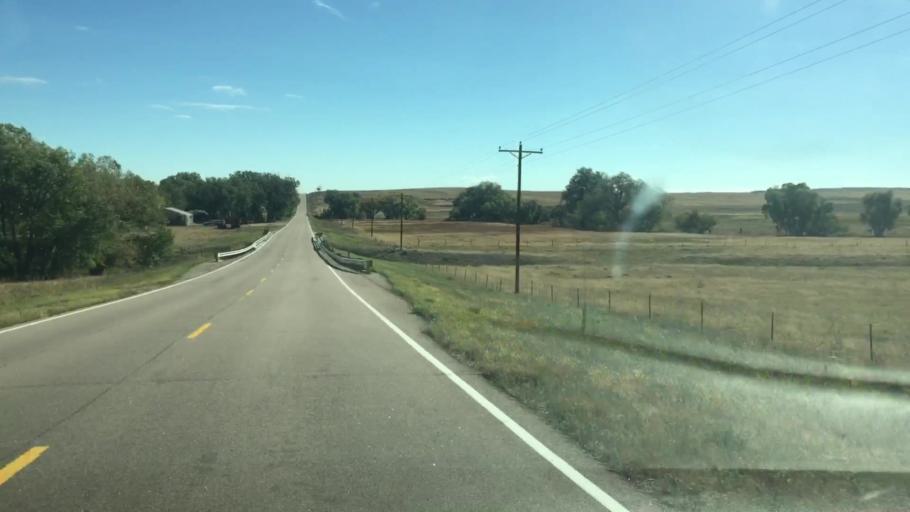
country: US
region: Colorado
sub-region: Elbert County
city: Kiowa
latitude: 39.2737
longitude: -104.1155
